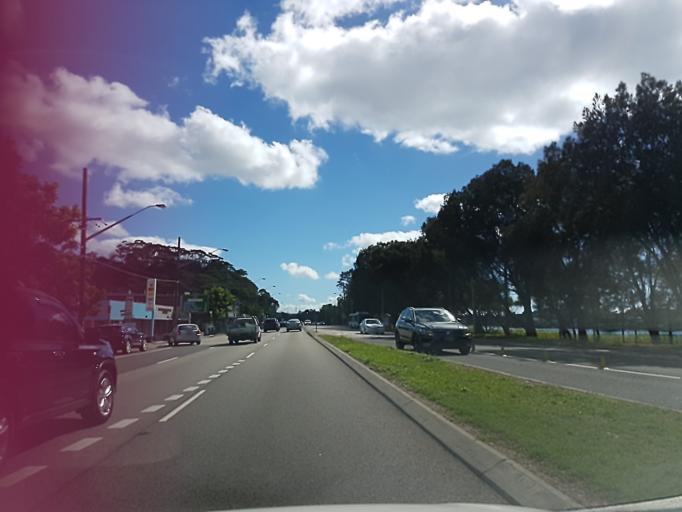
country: AU
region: New South Wales
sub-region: Pittwater
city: North Narrabeen
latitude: -33.7091
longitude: 151.2961
